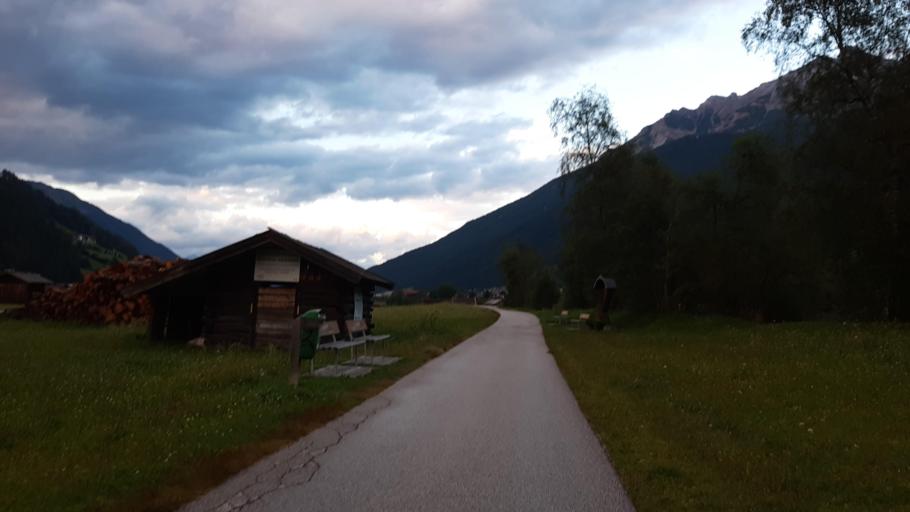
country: AT
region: Tyrol
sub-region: Politischer Bezirk Innsbruck Land
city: Neustift im Stubaital
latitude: 47.1126
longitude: 11.3165
